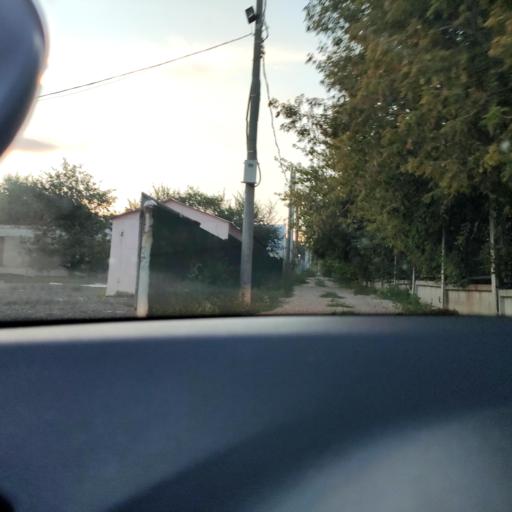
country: RU
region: Samara
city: Petra-Dubrava
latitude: 53.2609
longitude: 50.2853
